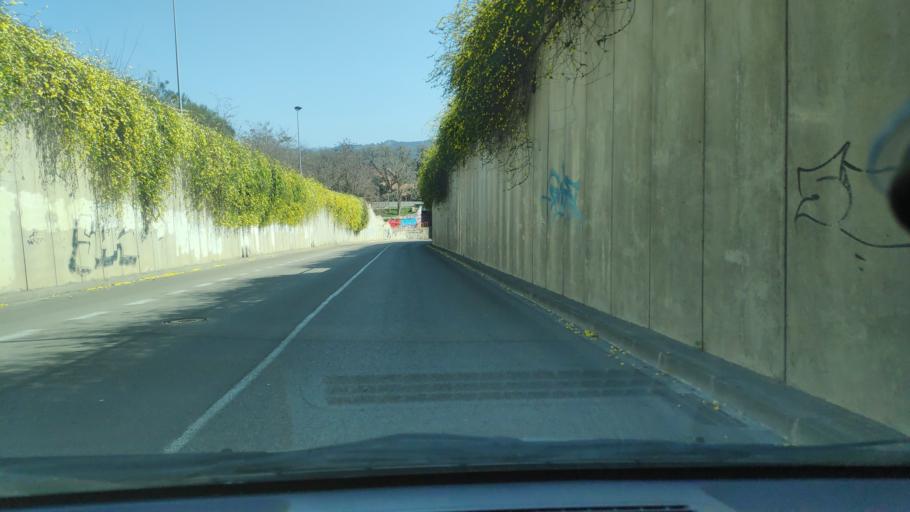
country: ES
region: Catalonia
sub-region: Provincia de Barcelona
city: Mollet del Valles
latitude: 41.5476
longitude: 2.2148
